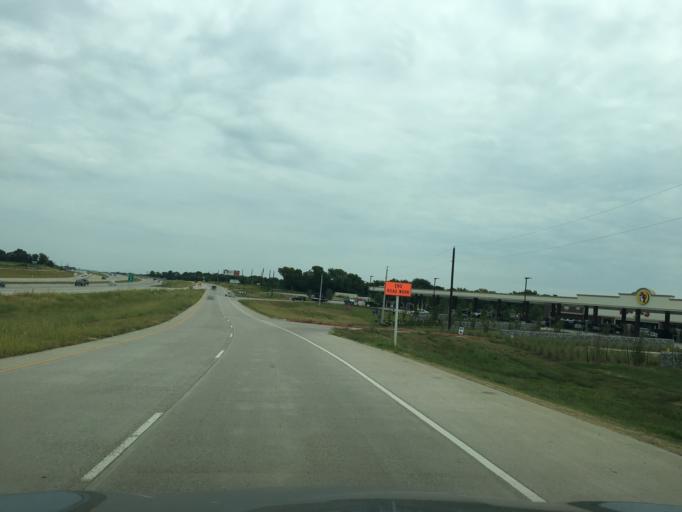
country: US
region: Texas
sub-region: Collin County
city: Melissa
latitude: 33.2706
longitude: -96.5936
